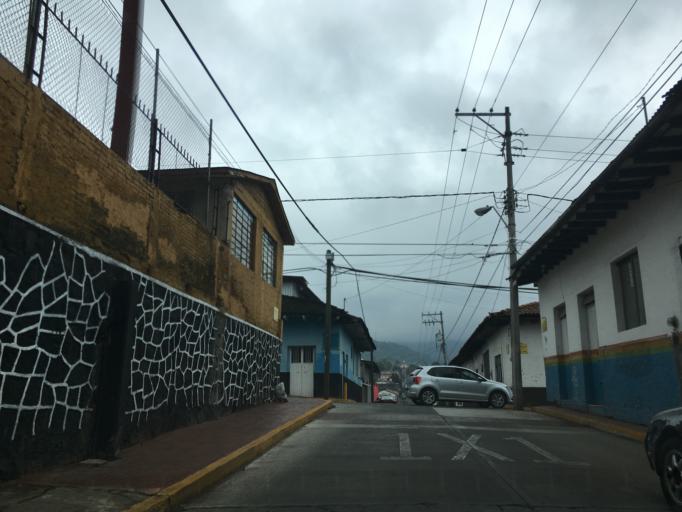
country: MX
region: Michoacan
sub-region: Uruapan
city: Uruapan
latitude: 19.4149
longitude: -102.0658
